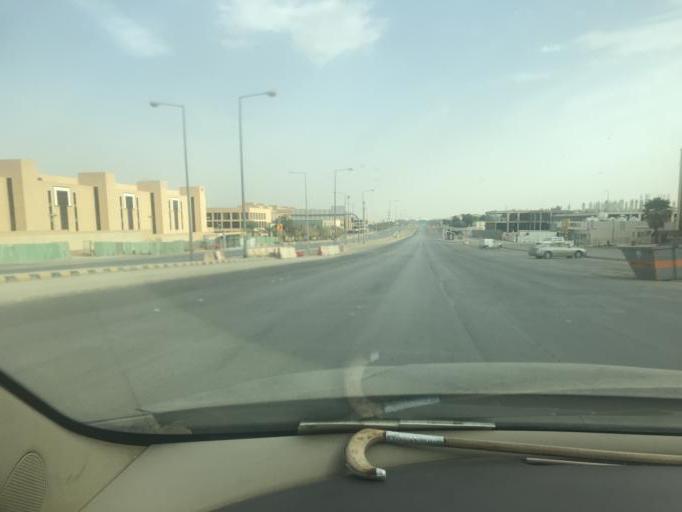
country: SA
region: Ar Riyad
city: Riyadh
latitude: 24.8151
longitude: 46.6890
